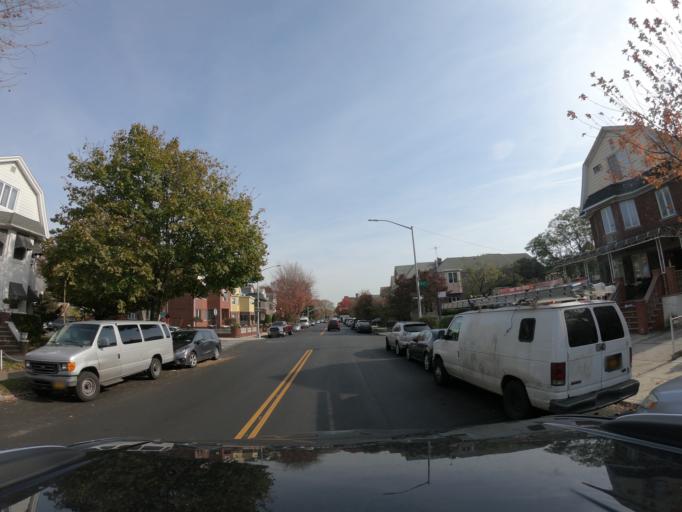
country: US
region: New York
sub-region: Kings County
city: Bensonhurst
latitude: 40.6115
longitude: -73.9727
